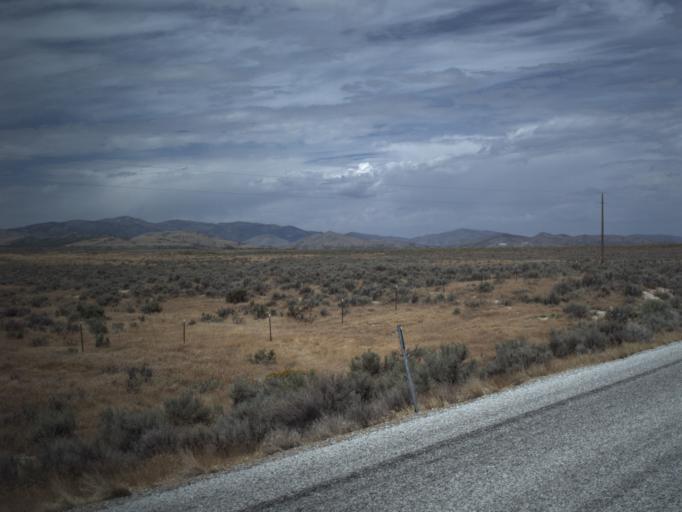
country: US
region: Utah
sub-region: Tooele County
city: Wendover
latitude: 41.5327
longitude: -113.5931
